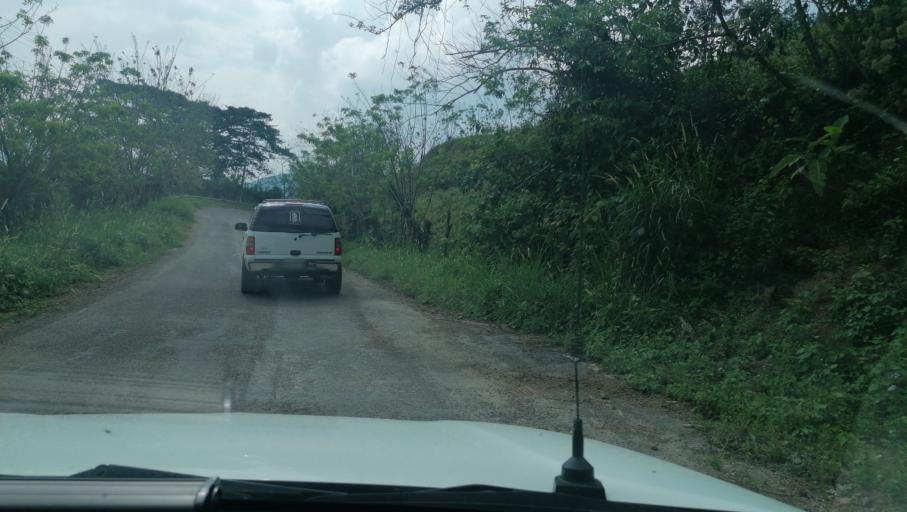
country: MX
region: Chiapas
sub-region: Francisco Leon
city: San Miguel la Sardina
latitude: 17.2332
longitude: -93.3336
